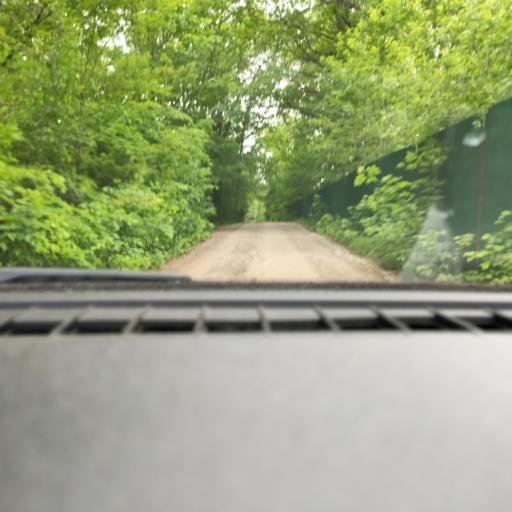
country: RU
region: Samara
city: Volzhskiy
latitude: 53.4212
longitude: 50.1126
